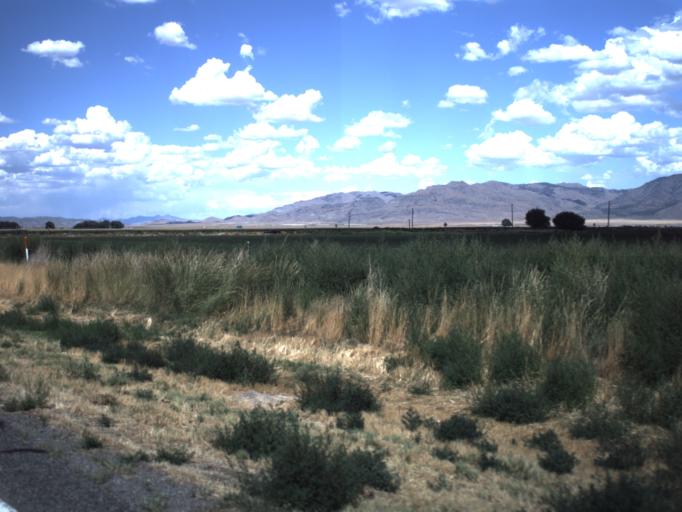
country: US
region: Utah
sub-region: Millard County
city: Delta
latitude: 39.5226
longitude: -112.3720
